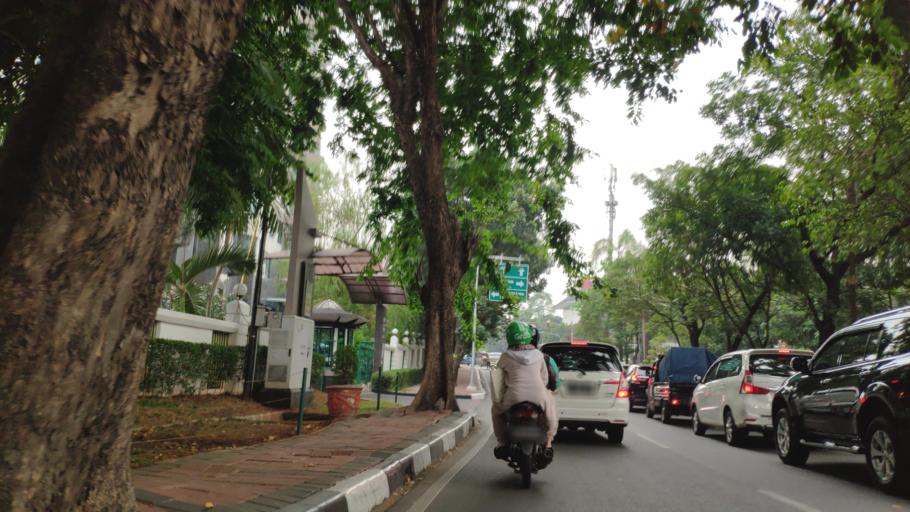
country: ID
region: Jakarta Raya
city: Jakarta
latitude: -6.2455
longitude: 106.7880
